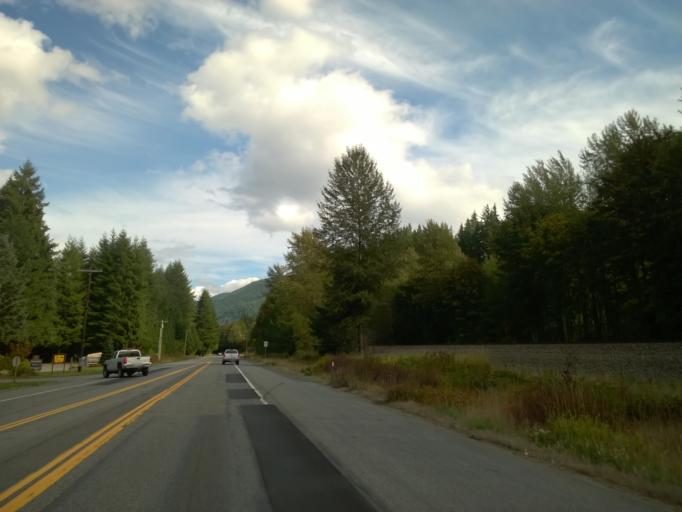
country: US
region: Washington
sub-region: Snohomish County
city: Gold Bar
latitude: 47.7128
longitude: -121.3327
